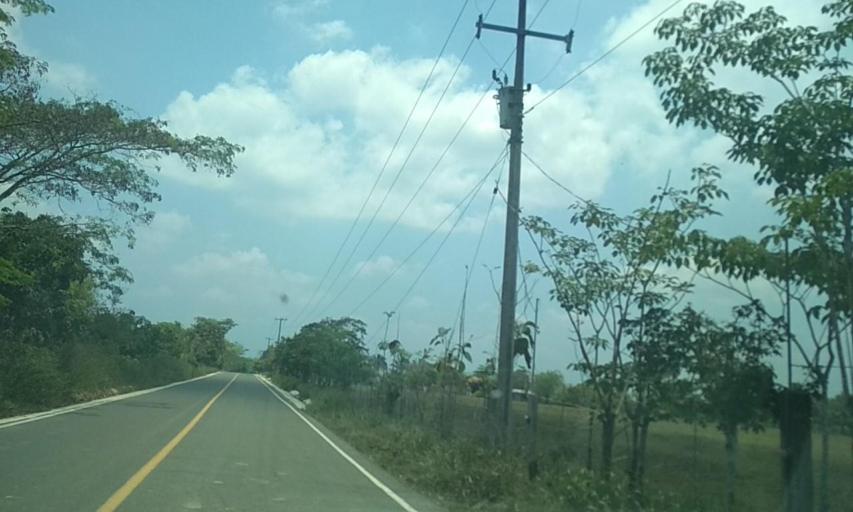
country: MX
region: Tabasco
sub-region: Huimanguillo
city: Francisco Rueda
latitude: 17.7493
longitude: -94.0369
